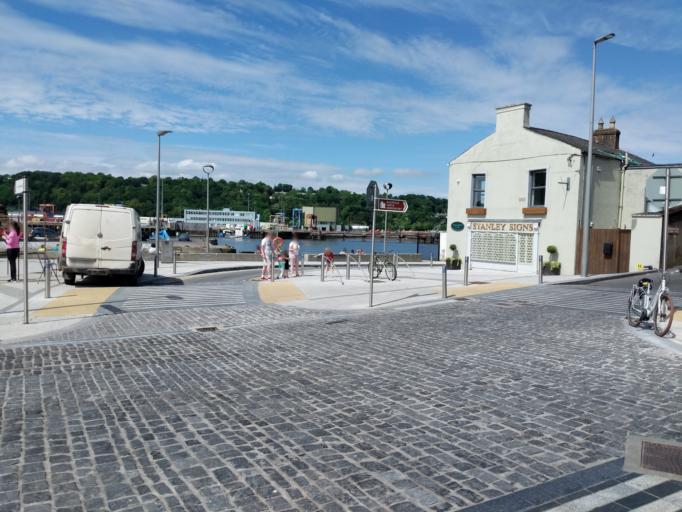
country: IE
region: Munster
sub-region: County Cork
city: Cork
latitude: 51.8973
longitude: -8.4128
